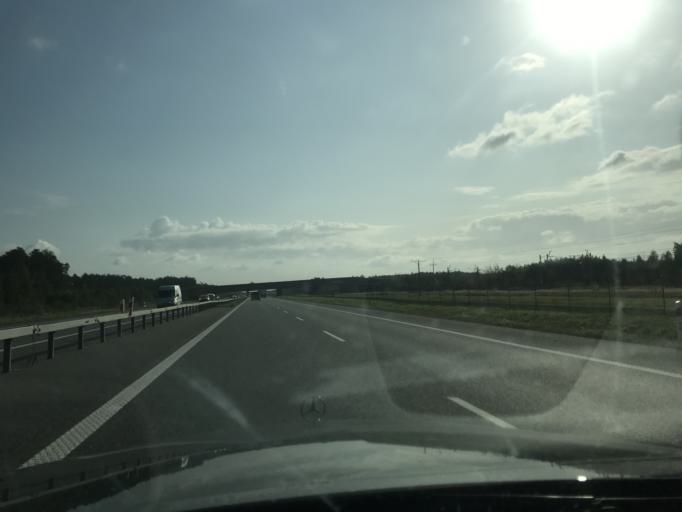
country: PL
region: Lesser Poland Voivodeship
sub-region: Powiat tarnowski
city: Wojnicz
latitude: 50.0058
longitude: 20.7832
